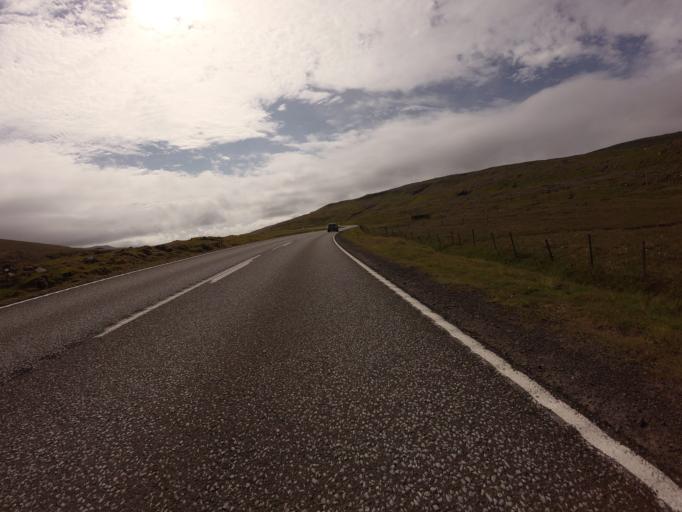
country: FO
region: Sandoy
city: Sandur
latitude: 61.8843
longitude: -6.8662
